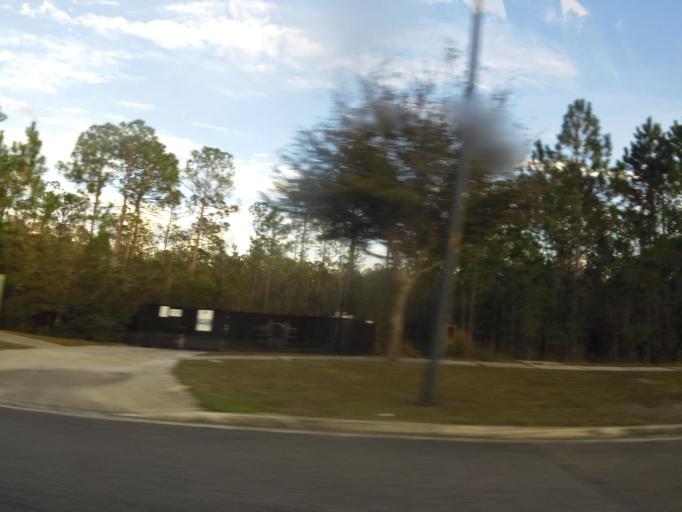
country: US
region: Florida
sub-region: Duval County
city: Baldwin
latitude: 30.2529
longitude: -81.8864
